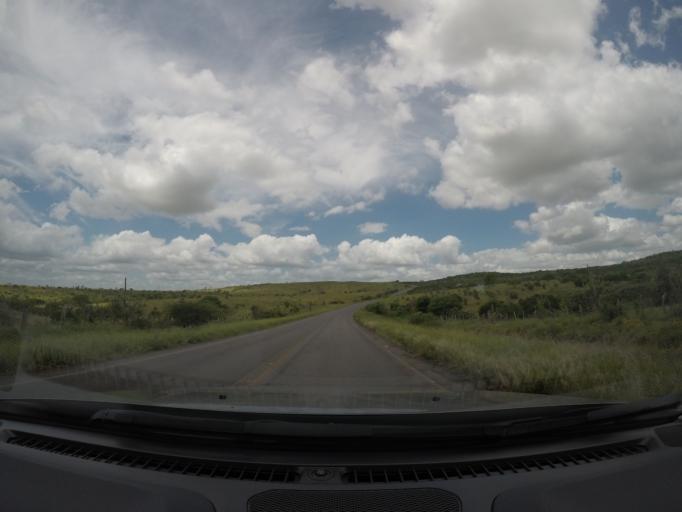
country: BR
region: Bahia
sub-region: Ipira
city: Ipira
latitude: -12.2569
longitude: -39.8229
